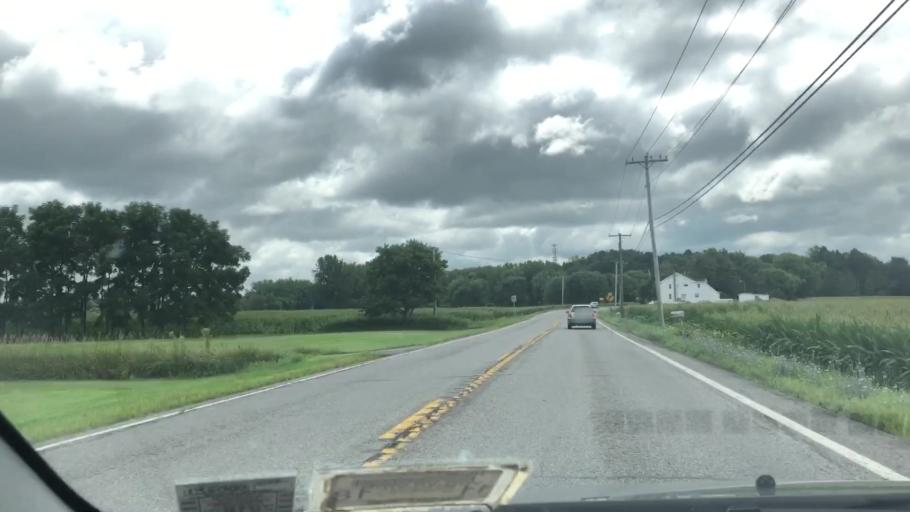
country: US
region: New York
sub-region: Wayne County
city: Macedon
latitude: 43.0992
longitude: -77.2941
